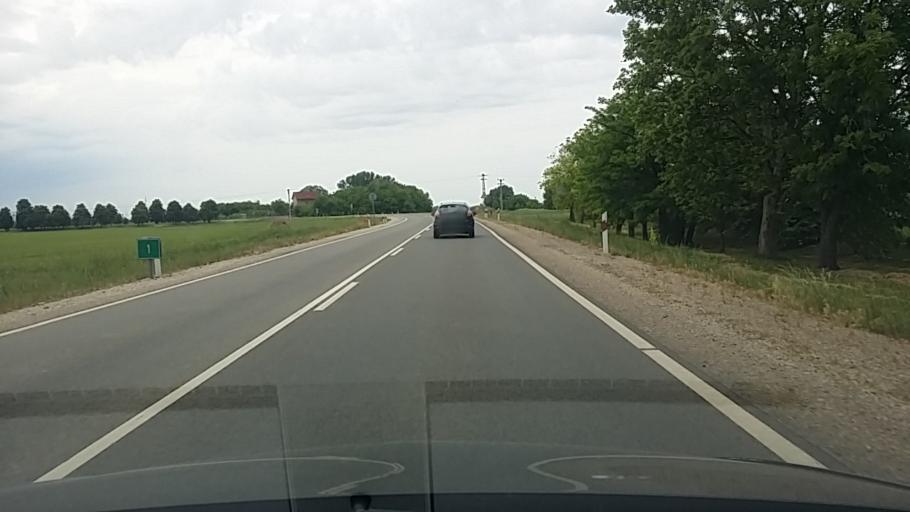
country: HU
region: Fejer
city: dunaujvaros
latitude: 46.9848
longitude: 18.9014
